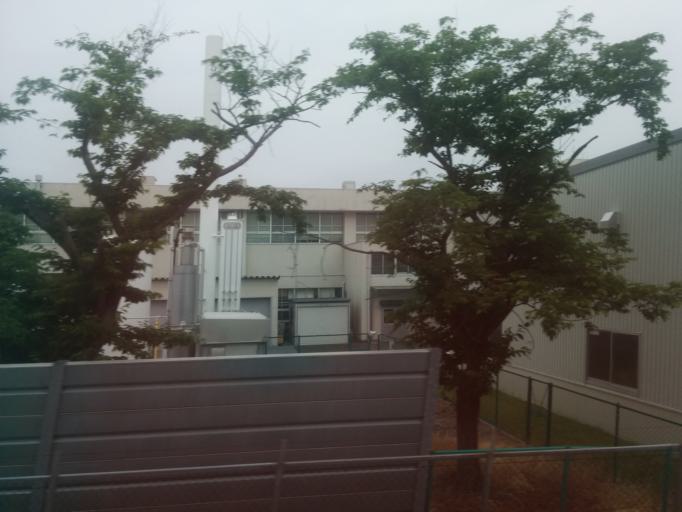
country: JP
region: Shiga Prefecture
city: Hikone
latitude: 35.2509
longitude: 136.2534
